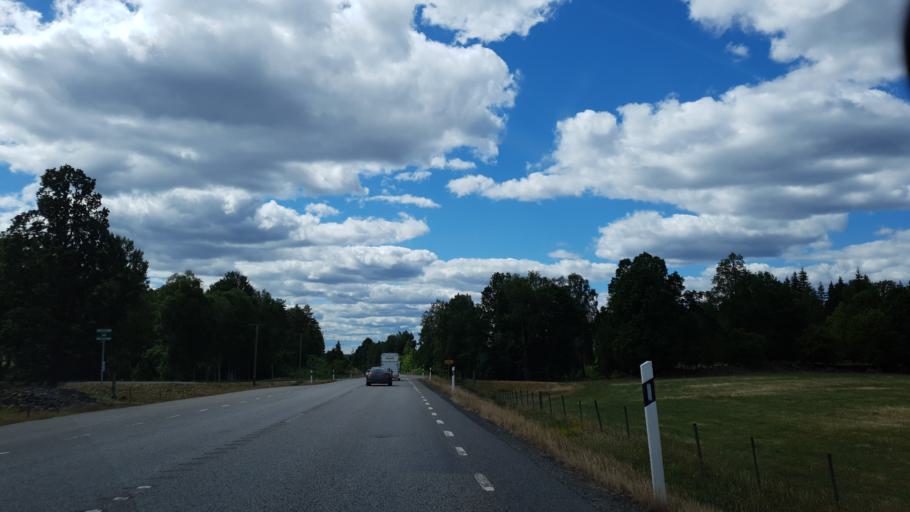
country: SE
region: Kronoberg
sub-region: Vaxjo Kommun
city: Braas
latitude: 57.1595
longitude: 15.1605
